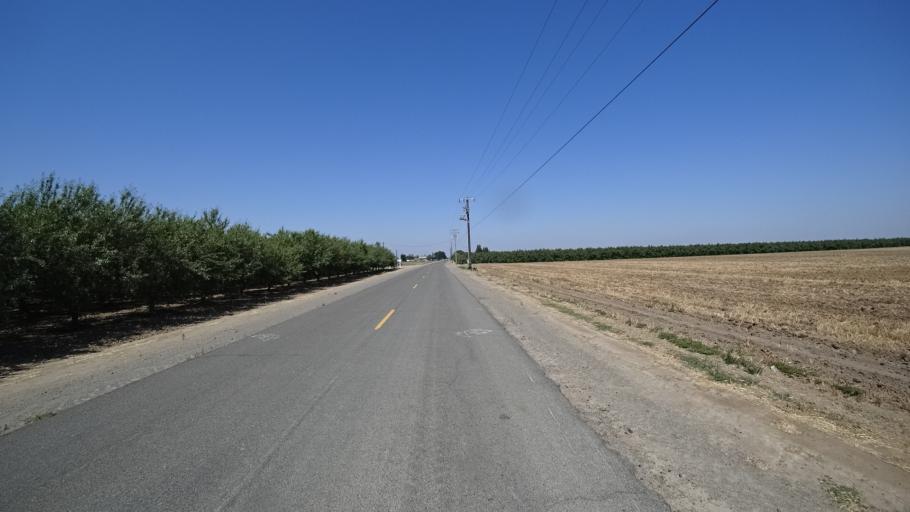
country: US
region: California
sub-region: Kings County
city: Hanford
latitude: 36.3716
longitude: -119.5996
